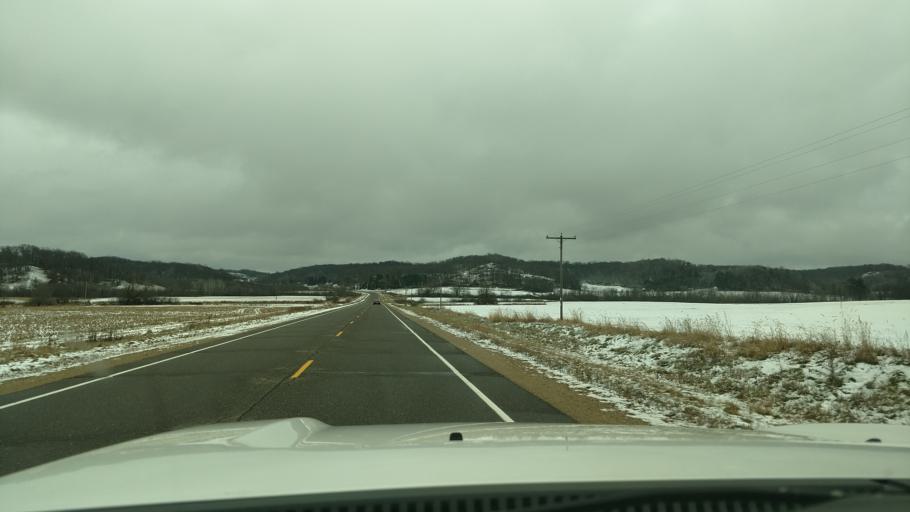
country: US
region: Wisconsin
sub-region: Dunn County
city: Tainter Lake
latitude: 45.1253
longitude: -91.8586
